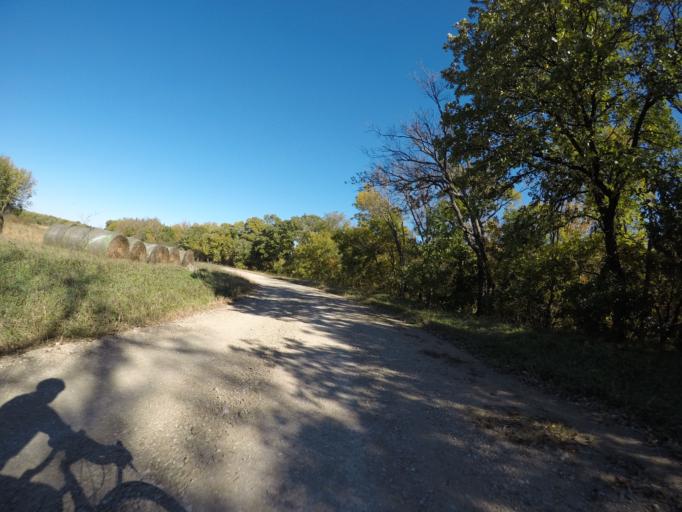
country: US
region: Kansas
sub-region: Wabaunsee County
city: Alma
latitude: 38.9383
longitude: -96.4007
